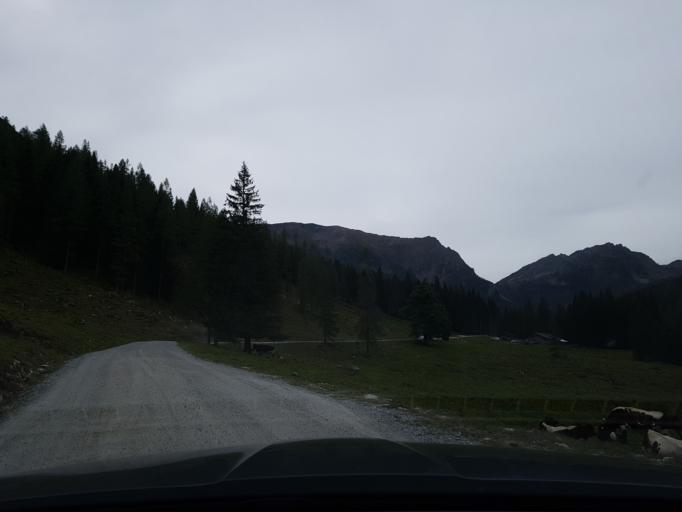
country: AT
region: Salzburg
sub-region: Politischer Bezirk Sankt Johann im Pongau
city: Forstau
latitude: 47.3051
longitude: 13.5819
